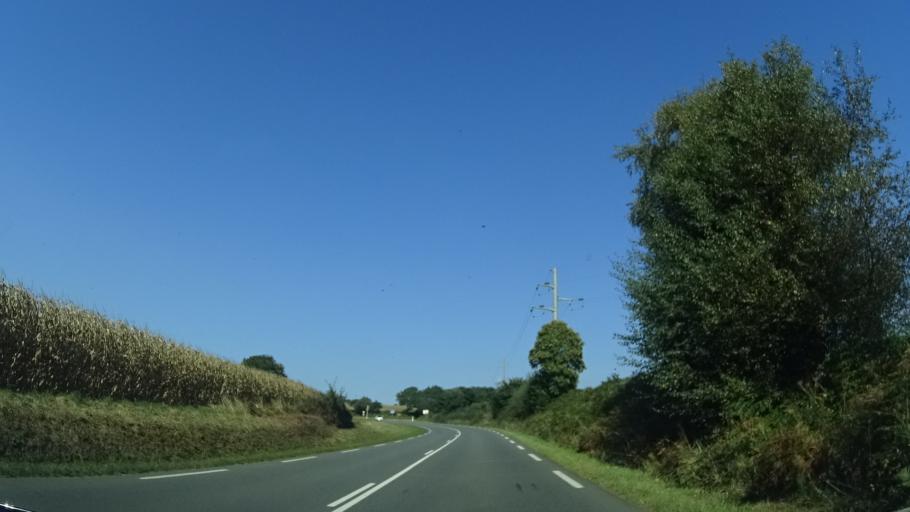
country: FR
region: Brittany
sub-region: Departement du Finistere
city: Plonevez-Porzay
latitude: 48.1121
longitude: -4.2408
